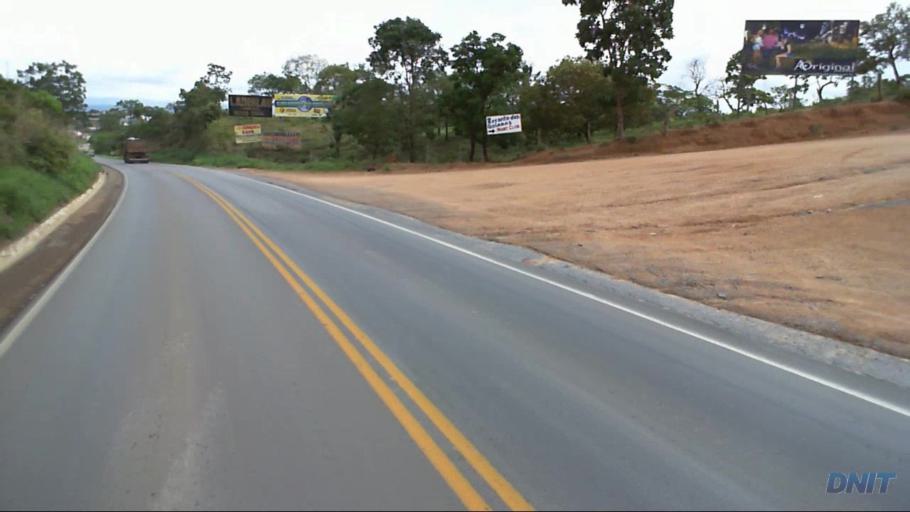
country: BR
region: Goias
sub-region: Padre Bernardo
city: Padre Bernardo
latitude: -15.1815
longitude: -48.2847
